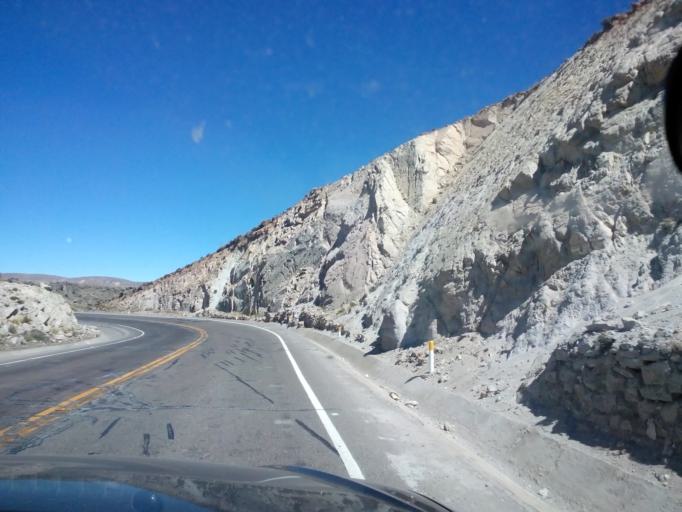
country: PE
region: Arequipa
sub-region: Provincia de Caylloma
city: Vizcachane
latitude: -15.9265
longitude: -71.1914
